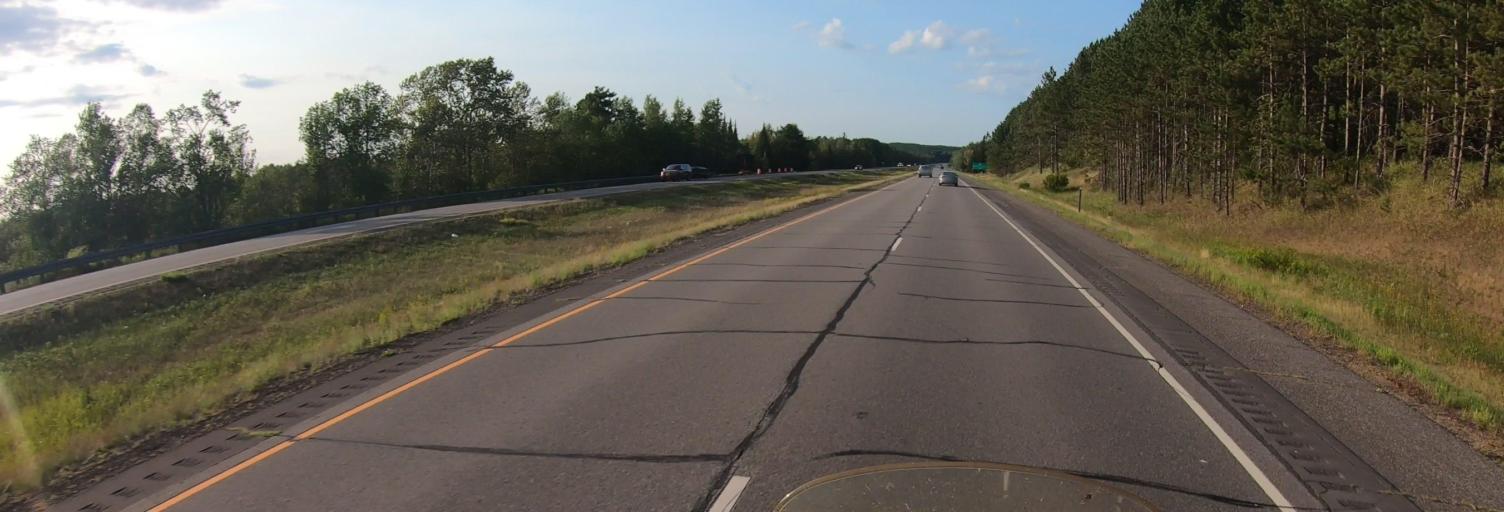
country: US
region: Minnesota
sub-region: Saint Louis County
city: Eveleth
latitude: 47.4238
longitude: -92.5216
